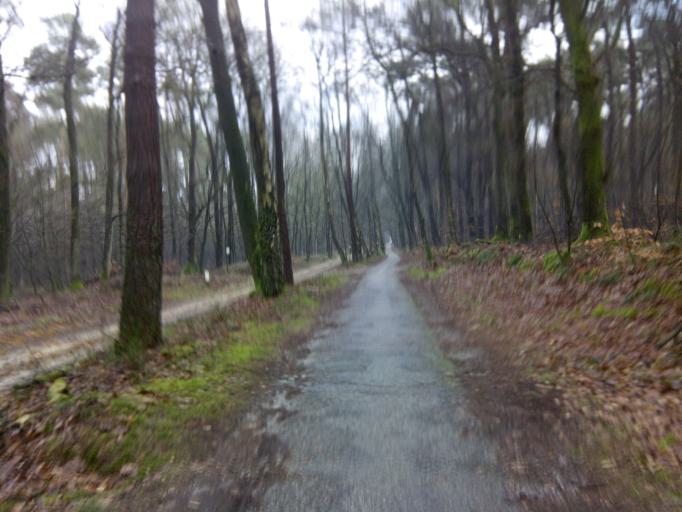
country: NL
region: Utrecht
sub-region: Gemeente Utrechtse Heuvelrug
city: Overberg
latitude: 52.0048
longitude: 5.4981
